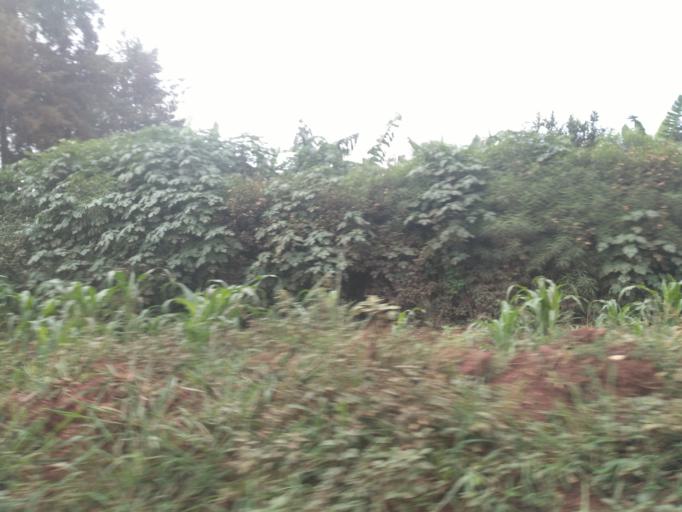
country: UG
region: Eastern Region
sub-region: Jinja District
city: Jinja
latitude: 0.4298
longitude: 33.1880
